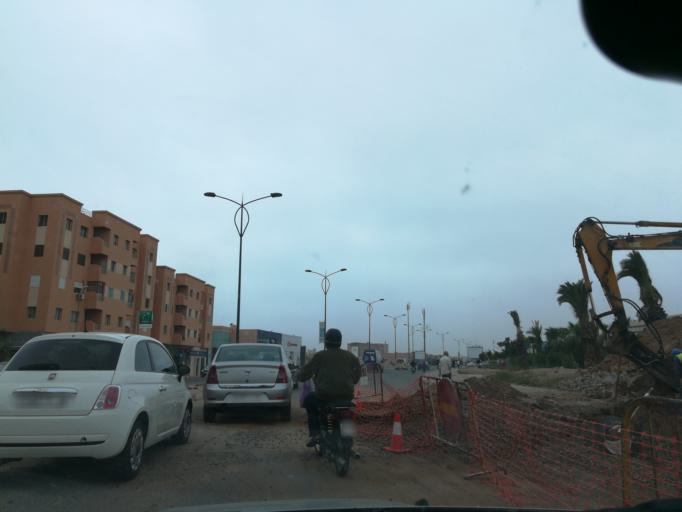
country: MA
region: Marrakech-Tensift-Al Haouz
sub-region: Marrakech
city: Marrakesh
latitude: 31.6718
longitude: -8.0146
